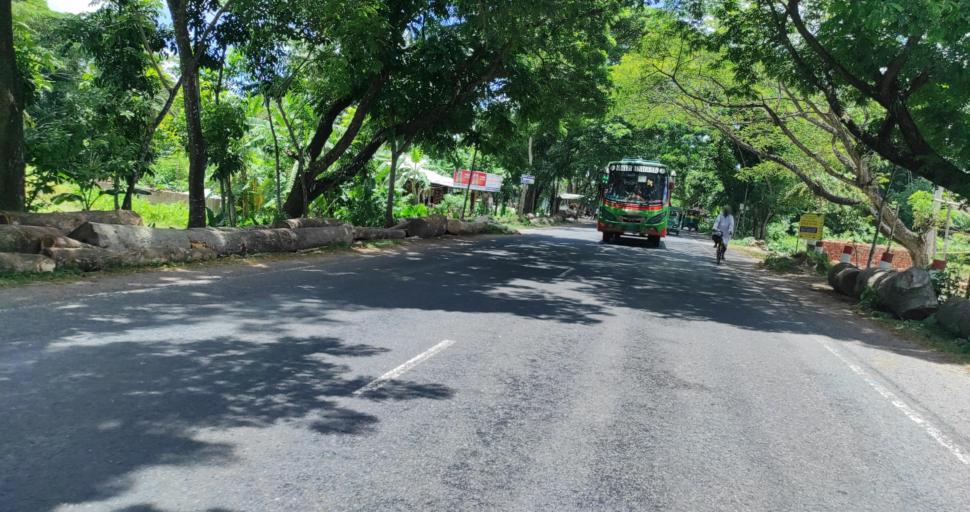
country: BD
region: Barisal
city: Gaurnadi
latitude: 22.8379
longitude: 90.2522
